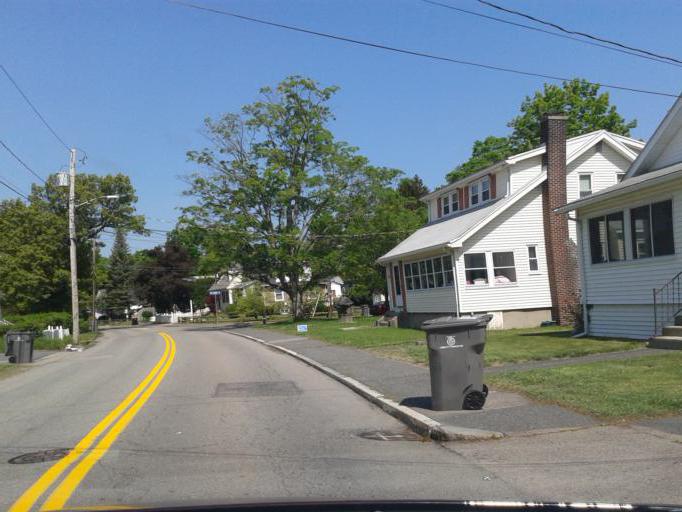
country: US
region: Massachusetts
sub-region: Middlesex County
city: Framingham
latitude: 42.2665
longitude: -71.4216
